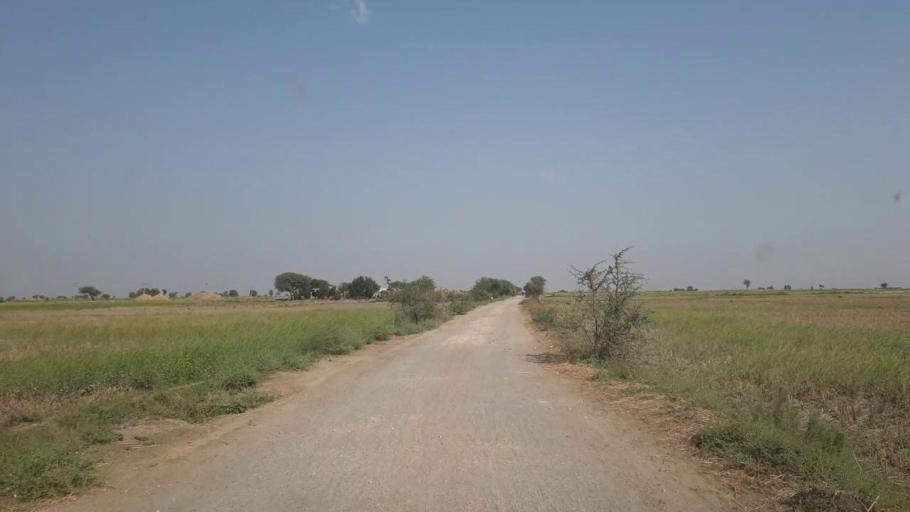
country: PK
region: Sindh
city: Kario
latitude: 24.5357
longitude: 68.5334
